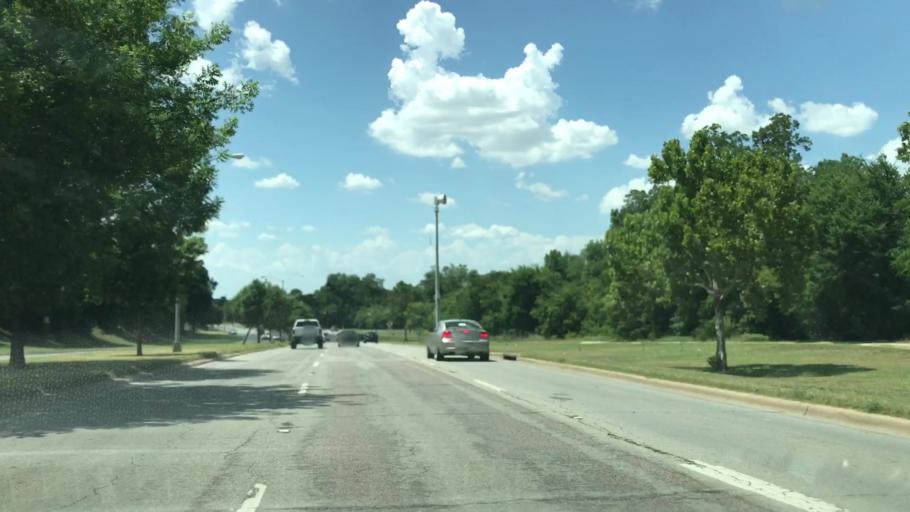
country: US
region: Texas
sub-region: Dallas County
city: University Park
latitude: 32.8575
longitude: -96.8486
